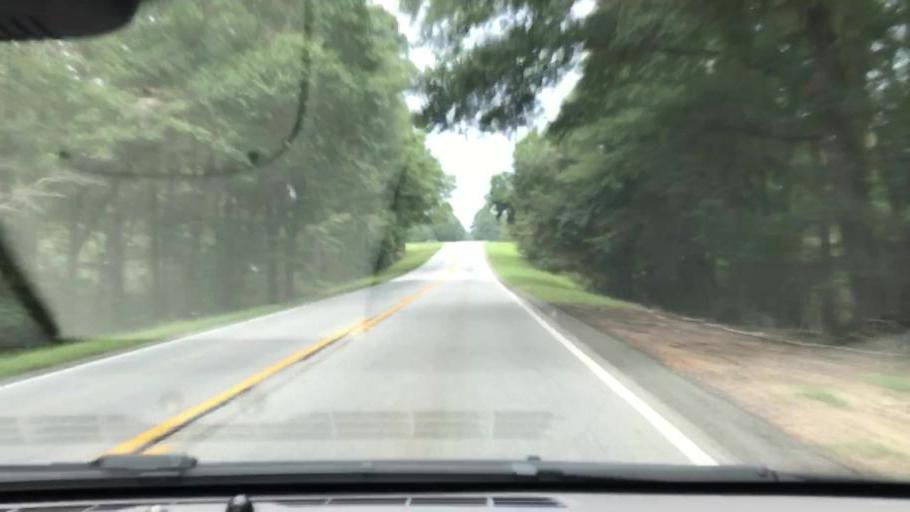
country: US
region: Georgia
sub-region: Early County
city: Blakely
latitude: 31.2803
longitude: -85.0799
